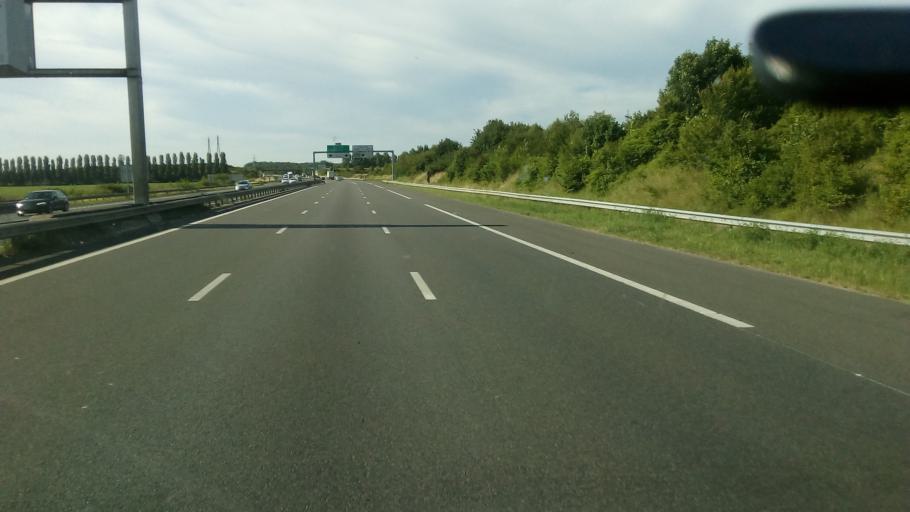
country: FR
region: Ile-de-France
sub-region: Departement de Seine-et-Marne
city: Vert-Saint-Denis
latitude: 48.5800
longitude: 2.6378
